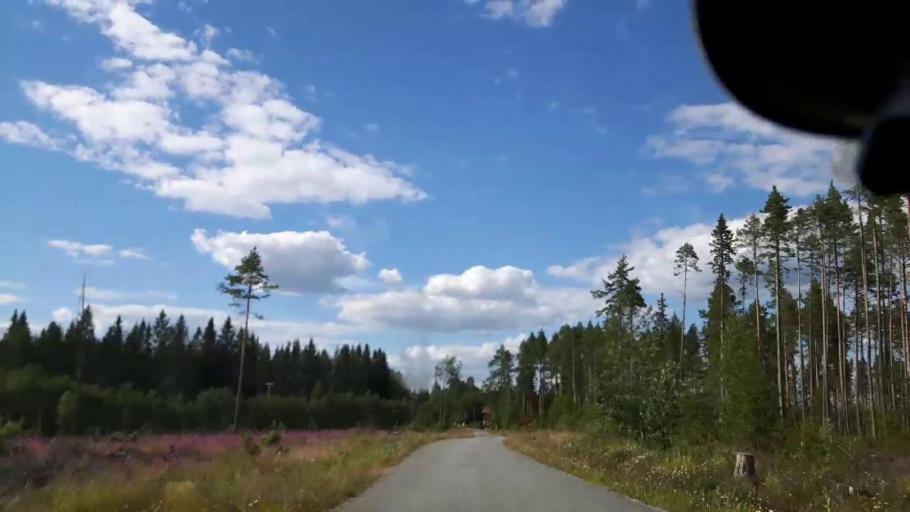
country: SE
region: Jaemtland
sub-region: Braecke Kommun
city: Braecke
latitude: 62.8387
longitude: 15.3025
